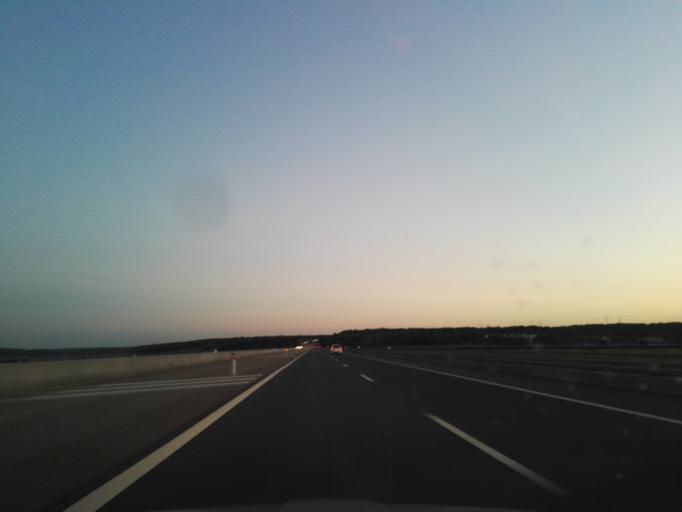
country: PT
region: Setubal
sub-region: Alcacer do Sal
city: Alcacer do Sal
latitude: 38.3634
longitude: -8.4907
